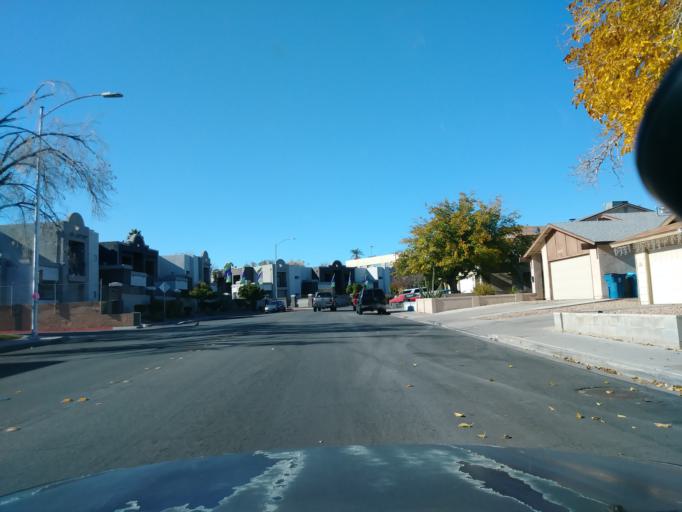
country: US
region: Nevada
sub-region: Clark County
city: Spring Valley
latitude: 36.1775
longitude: -115.2396
